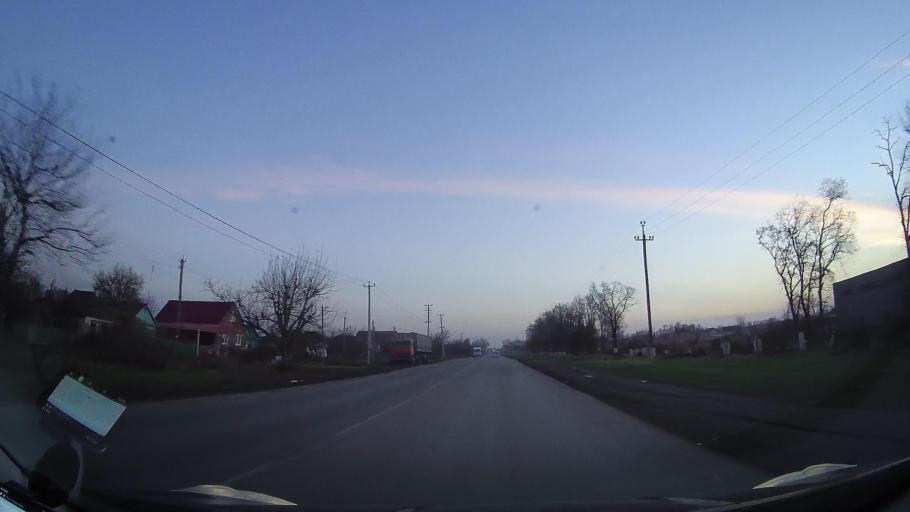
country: RU
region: Rostov
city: Zernograd
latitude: 46.8397
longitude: 40.2994
